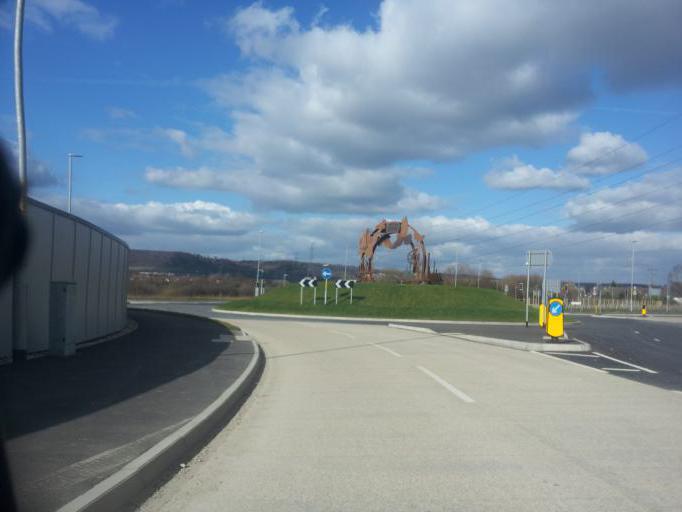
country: GB
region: England
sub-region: Medway
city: Halling
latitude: 51.3414
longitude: 0.4576
